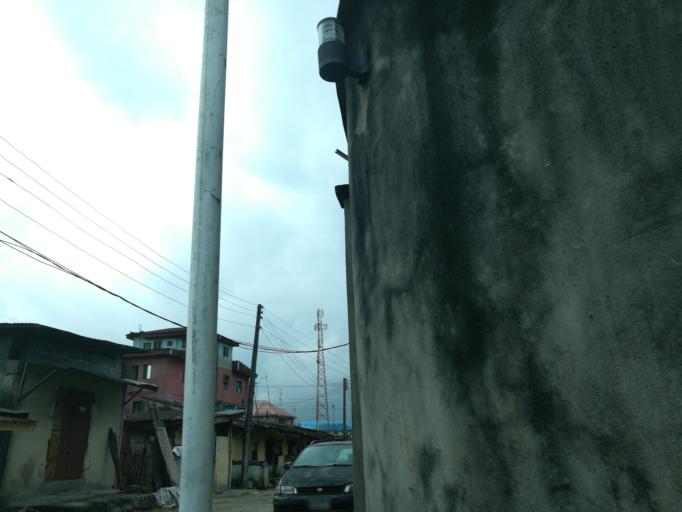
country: NG
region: Rivers
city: Port Harcourt
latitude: 4.8415
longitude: 7.0385
